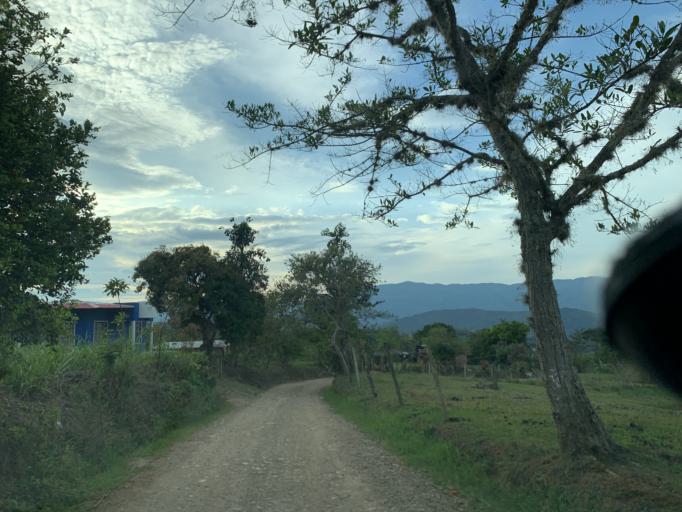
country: CO
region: Boyaca
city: Santana
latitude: 6.0806
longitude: -73.4914
